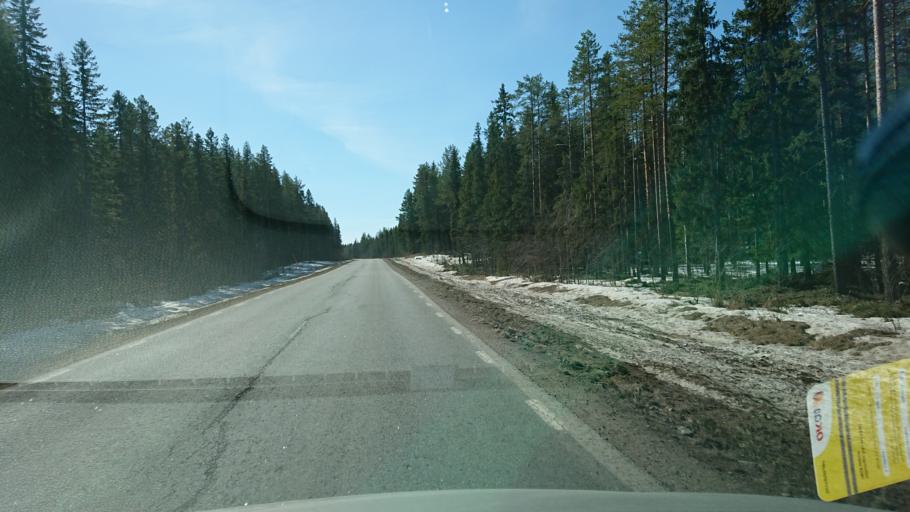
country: SE
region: Vaesternorrland
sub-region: Solleftea Kommun
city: As
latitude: 63.6252
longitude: 16.4378
